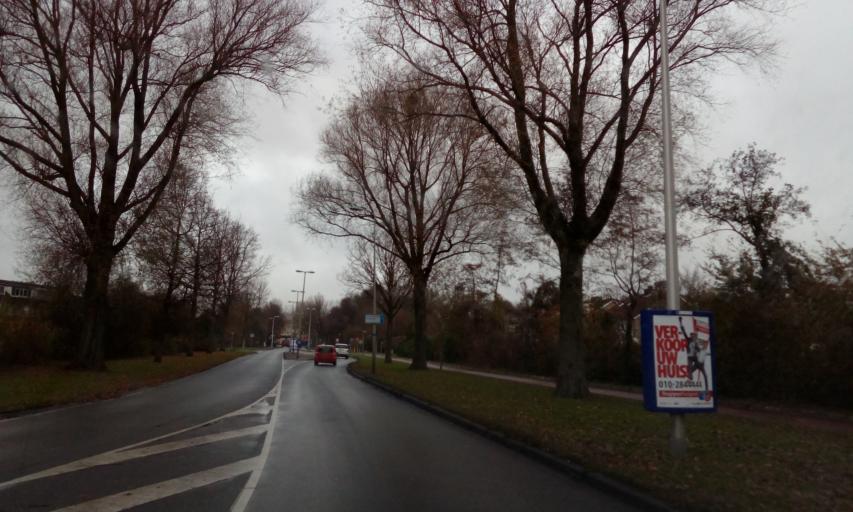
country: NL
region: South Holland
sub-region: Gemeente Capelle aan den IJssel
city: Capelle aan den IJssel
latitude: 51.9556
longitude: 4.5894
